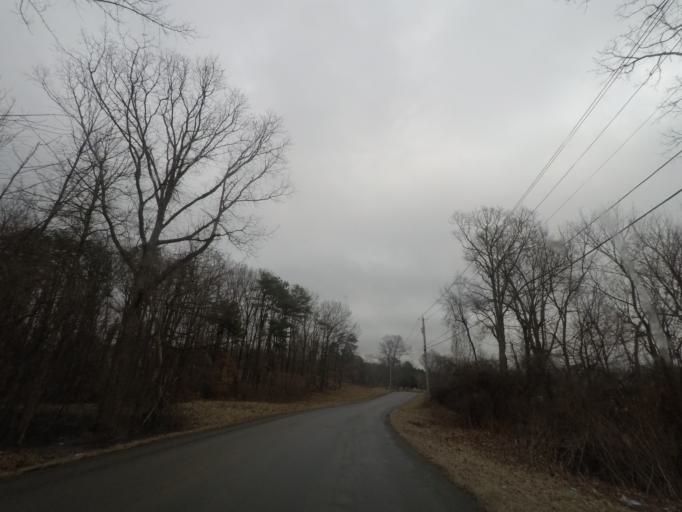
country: US
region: New York
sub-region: Saratoga County
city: Waterford
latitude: 42.7688
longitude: -73.6544
